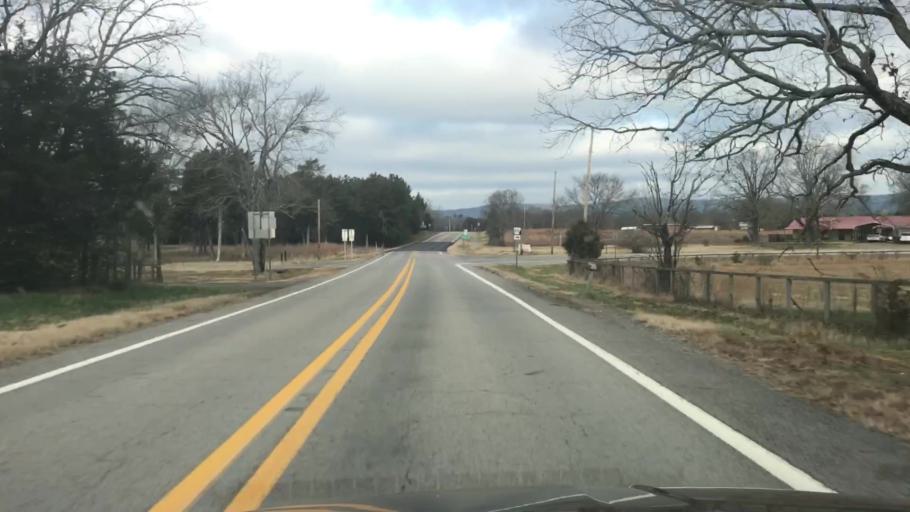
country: US
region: Arkansas
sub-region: Montgomery County
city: Mount Ida
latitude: 34.6336
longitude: -93.7367
